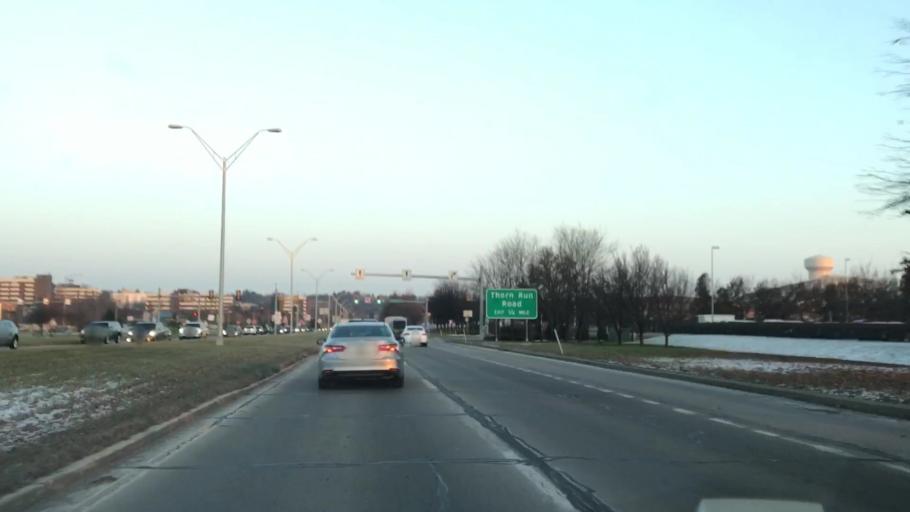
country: US
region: Pennsylvania
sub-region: Allegheny County
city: Carnot-Moon
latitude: 40.4999
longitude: -80.2208
